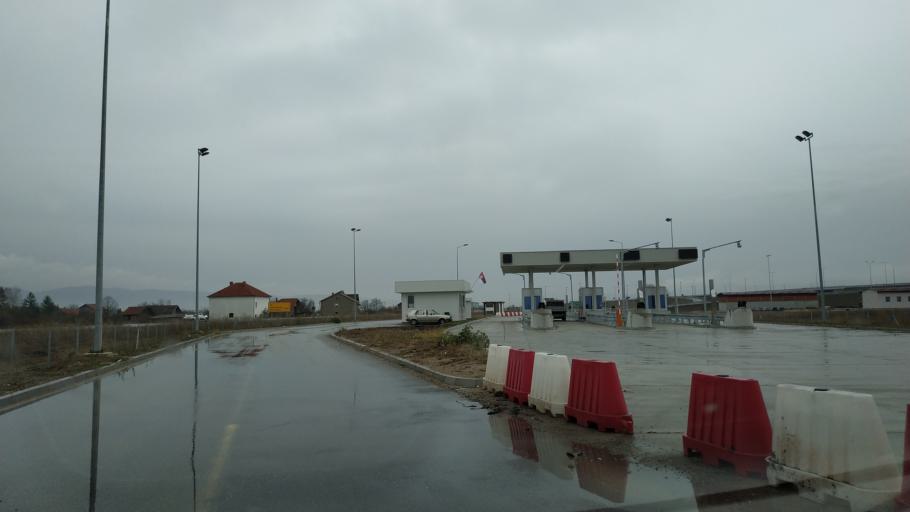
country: RS
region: Central Serbia
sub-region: Pirotski Okrug
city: Pirot
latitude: 43.1241
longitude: 22.6182
